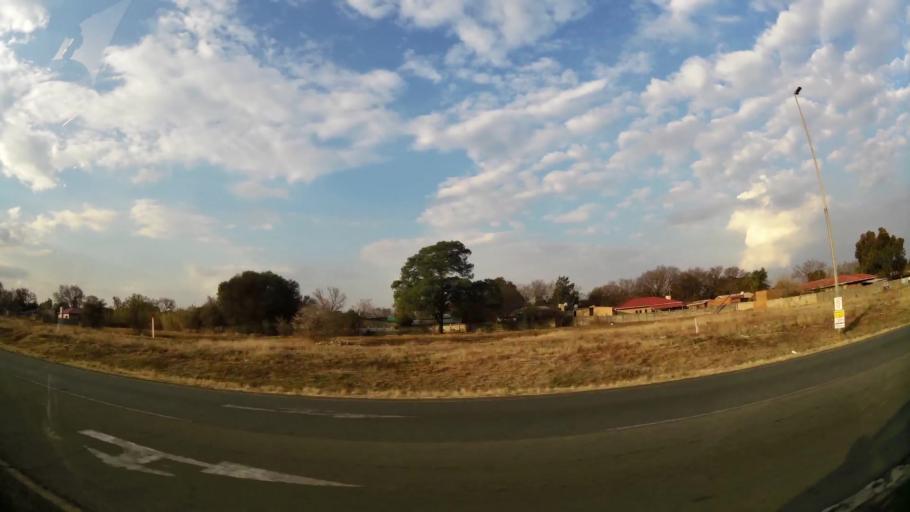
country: ZA
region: Gauteng
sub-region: Sedibeng District Municipality
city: Vanderbijlpark
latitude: -26.7028
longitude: 27.8116
